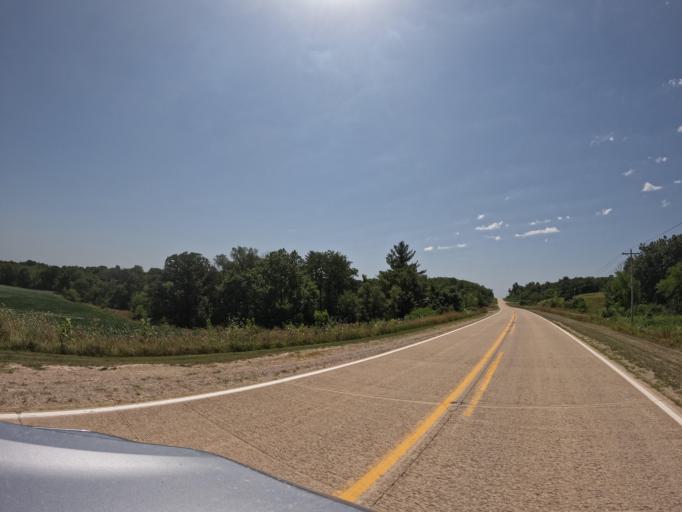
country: US
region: Iowa
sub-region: Henry County
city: Mount Pleasant
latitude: 40.9187
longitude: -91.5541
